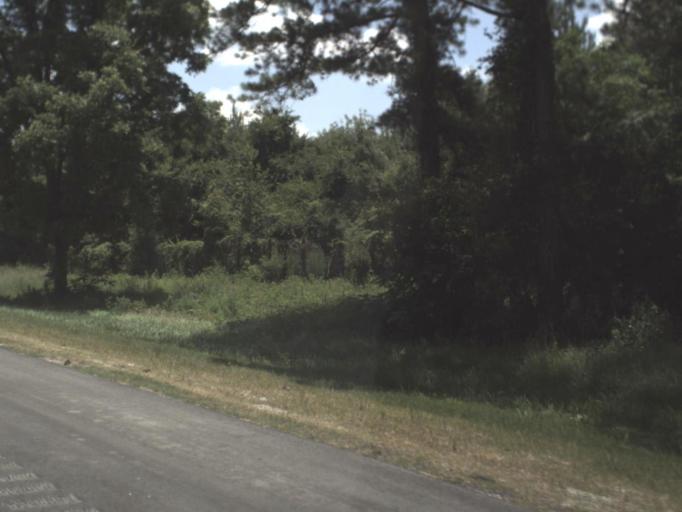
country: US
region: Florida
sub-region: Madison County
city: Madison
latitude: 30.4117
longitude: -83.4256
